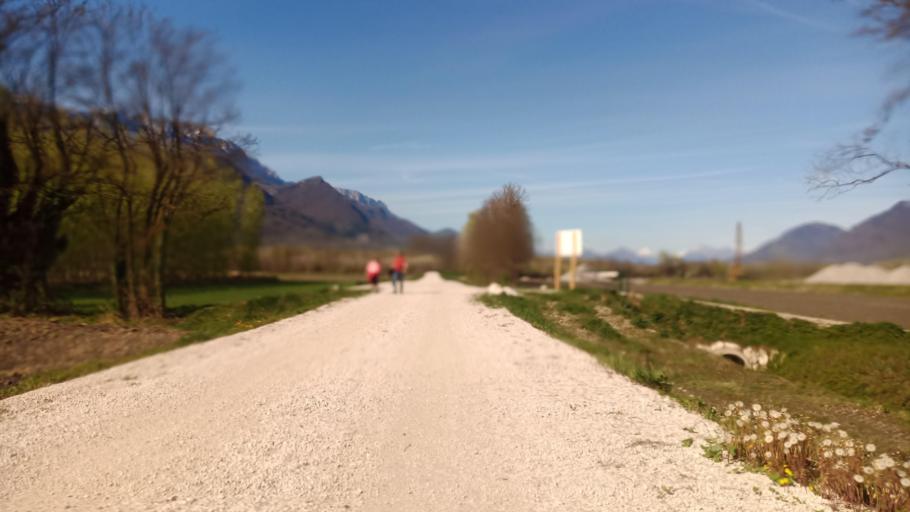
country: FR
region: Rhone-Alpes
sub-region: Departement de l'Isere
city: Froges
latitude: 45.2838
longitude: 5.9206
